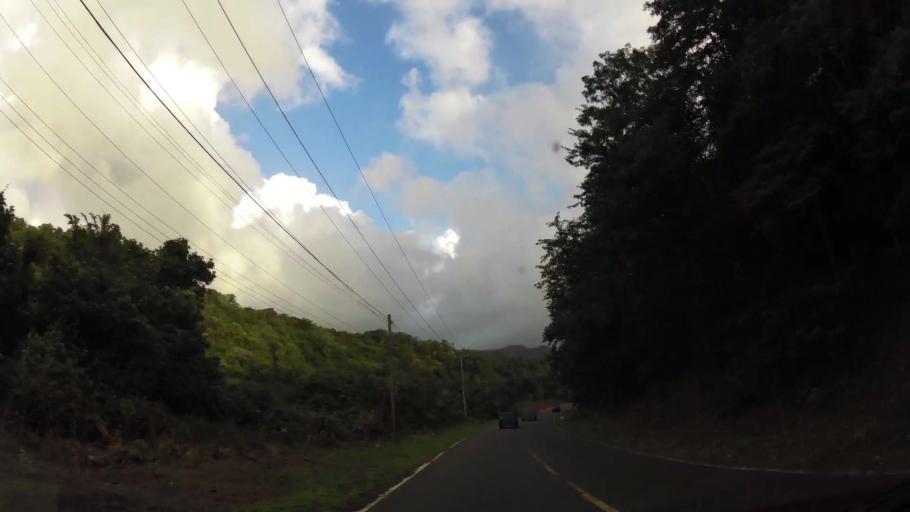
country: DM
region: Saint John
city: Portsmouth
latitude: 15.5452
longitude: -61.4710
